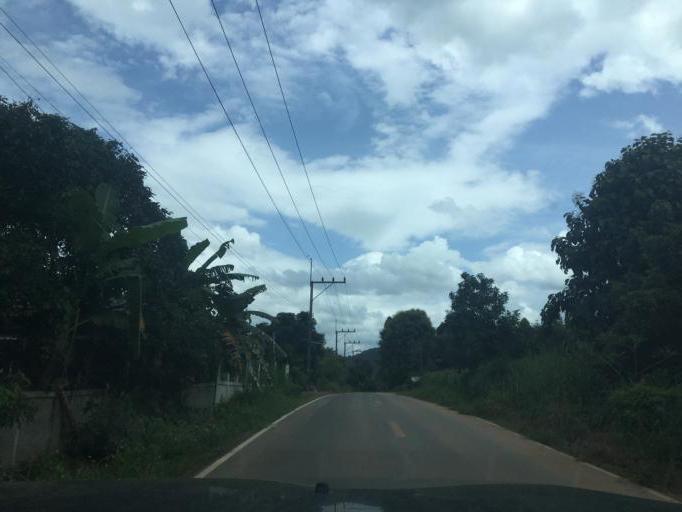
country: TH
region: Chiang Rai
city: Wiang Pa Pao
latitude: 19.2324
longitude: 99.4909
